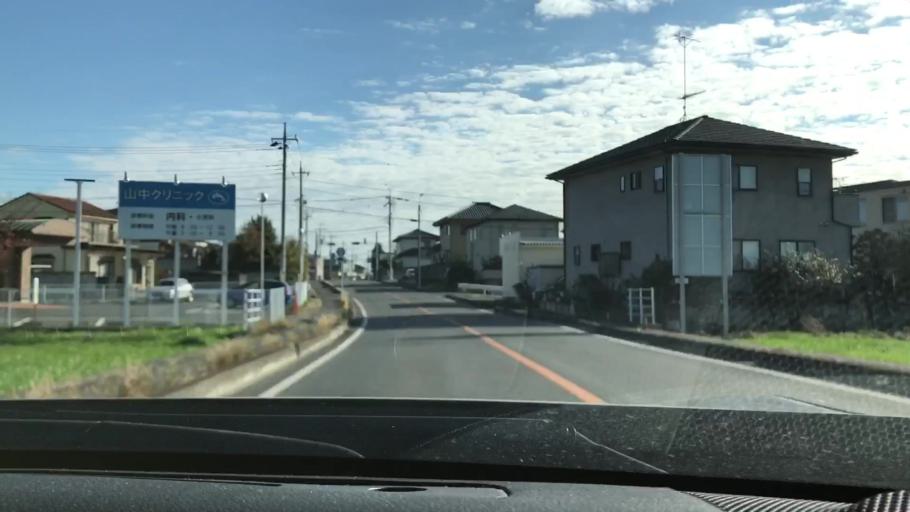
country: JP
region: Tochigi
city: Sano
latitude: 36.2986
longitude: 139.5752
